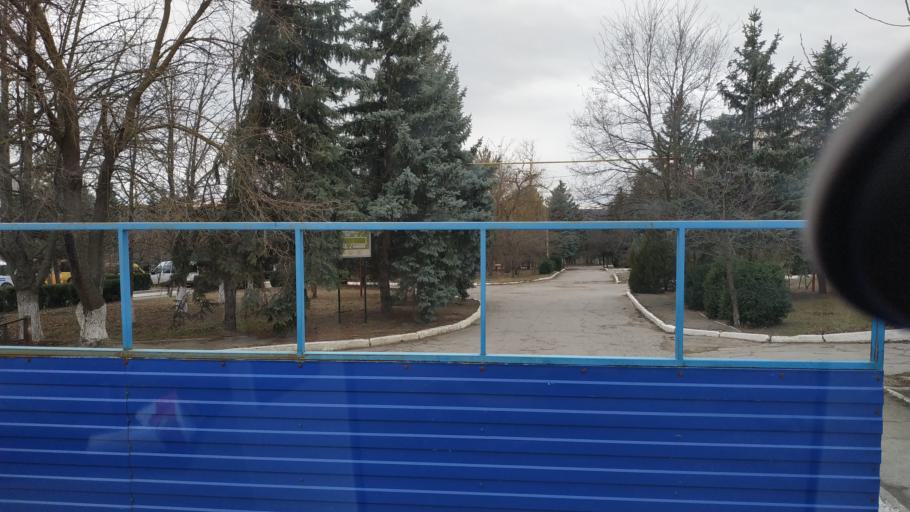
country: MD
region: Telenesti
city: Cocieri
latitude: 47.2918
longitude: 29.1200
